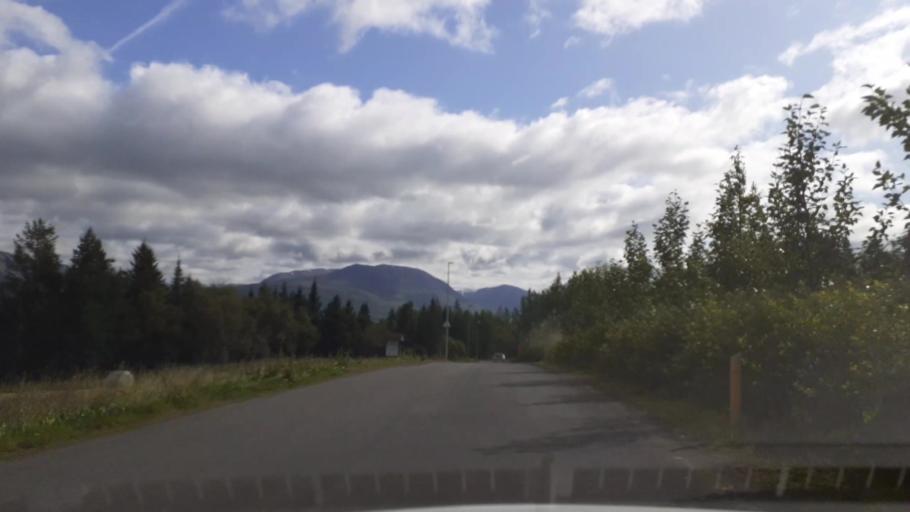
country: IS
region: Northeast
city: Akureyri
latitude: 65.6486
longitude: -18.0878
